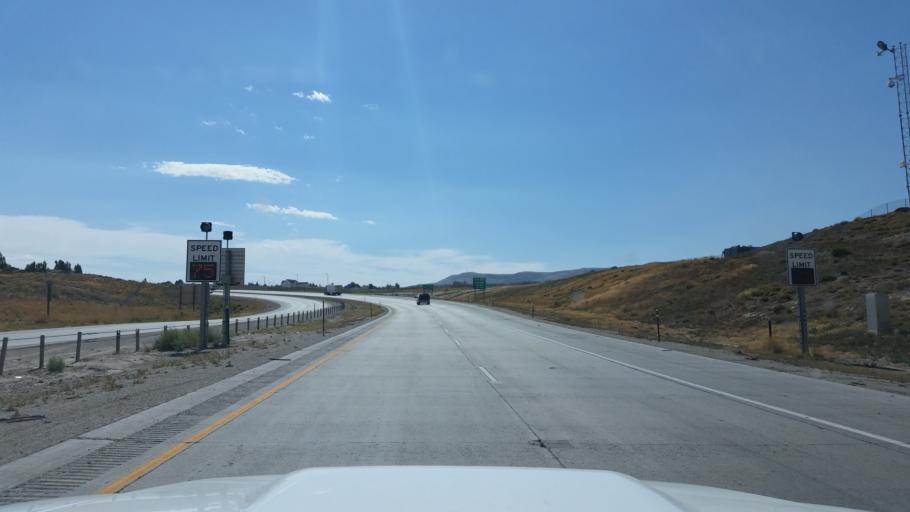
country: US
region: Wyoming
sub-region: Sweetwater County
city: Rock Springs
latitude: 41.6061
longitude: -109.2340
